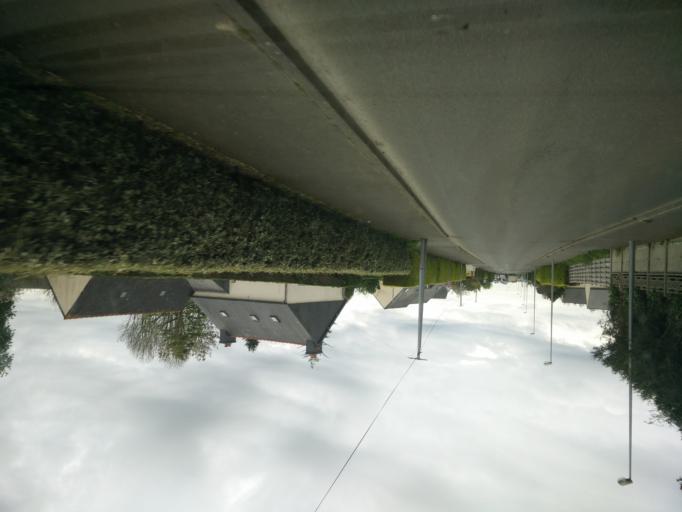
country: FR
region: Brittany
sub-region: Departement des Cotes-d'Armor
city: Lannion
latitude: 48.7248
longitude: -3.4816
